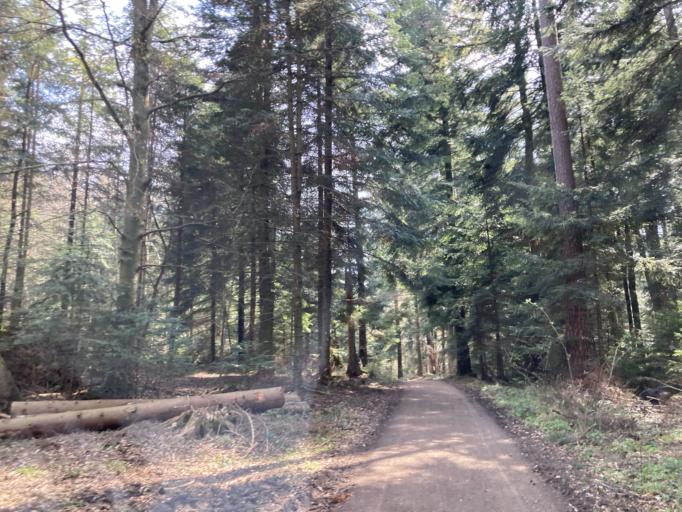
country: DE
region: Baden-Wuerttemberg
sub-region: Karlsruhe Region
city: Dobel
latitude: 48.8381
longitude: 8.5217
